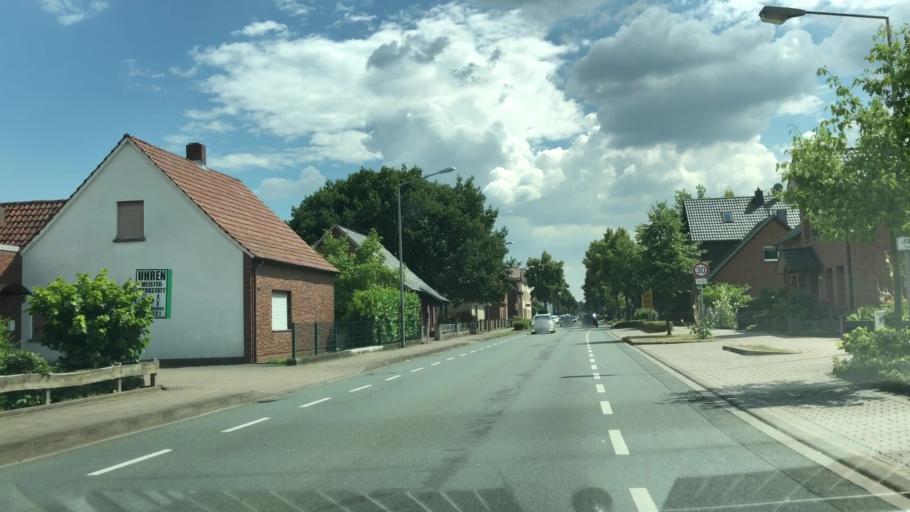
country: DE
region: North Rhine-Westphalia
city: Porta Westfalica
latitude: 52.2609
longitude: 8.9069
